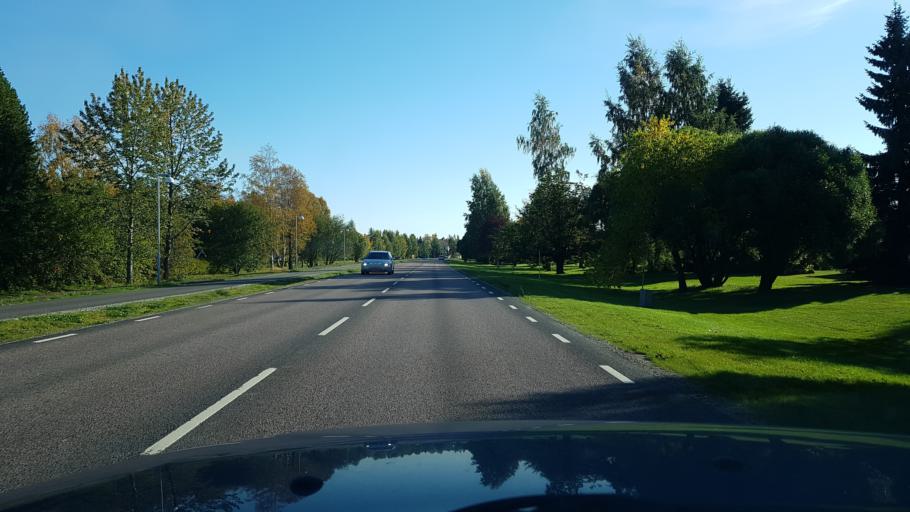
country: SE
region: Norrbotten
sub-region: Pitea Kommun
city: Pitea
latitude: 65.3235
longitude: 21.4559
